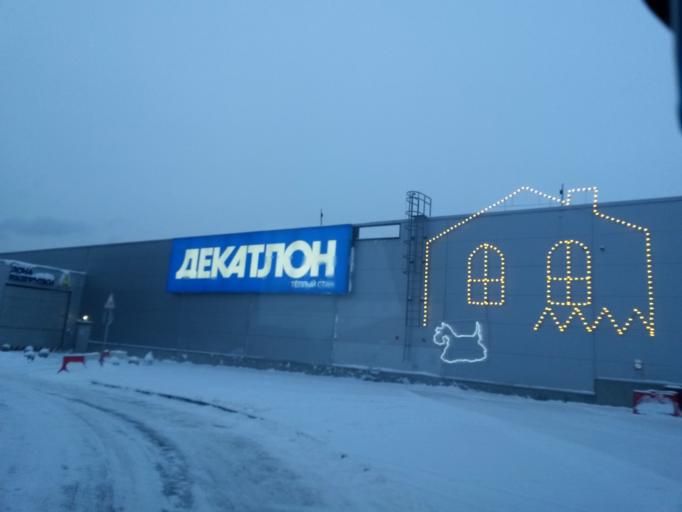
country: RU
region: Moscow
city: Tyoply Stan
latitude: 55.6054
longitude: 37.4907
